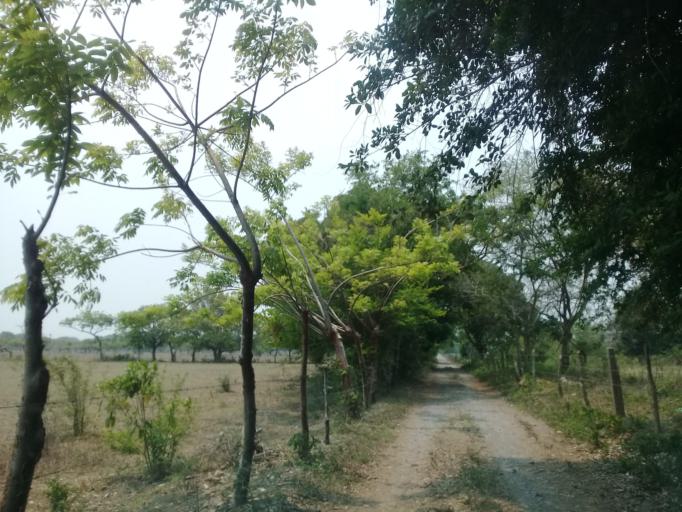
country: MX
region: Veracruz
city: Jamapa
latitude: 18.9259
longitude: -96.2022
